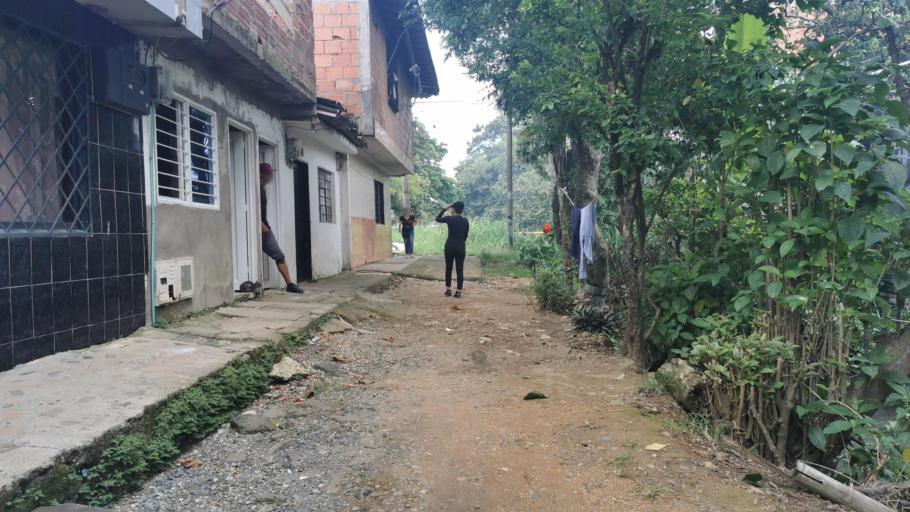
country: CO
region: Valle del Cauca
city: Jamundi
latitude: 3.2660
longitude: -76.5393
